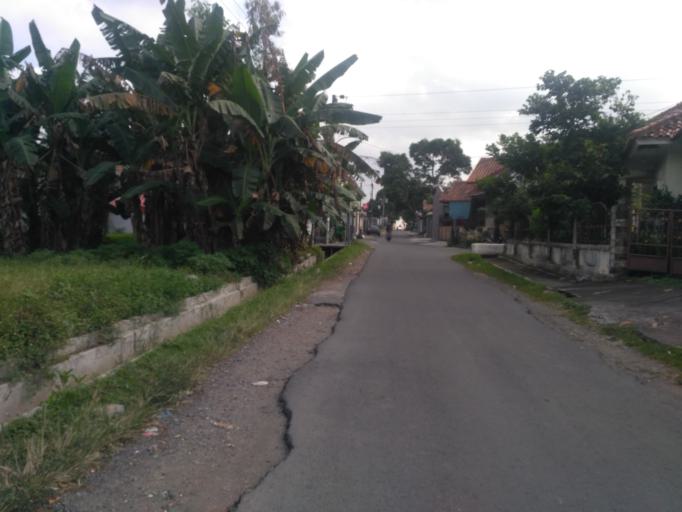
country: ID
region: Daerah Istimewa Yogyakarta
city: Yogyakarta
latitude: -7.7660
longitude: 110.3590
